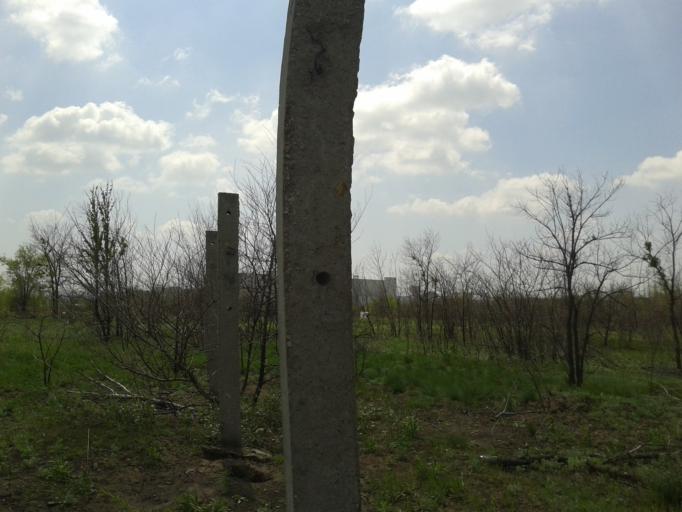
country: RU
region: Volgograd
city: Volgograd
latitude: 48.6423
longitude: 44.4389
